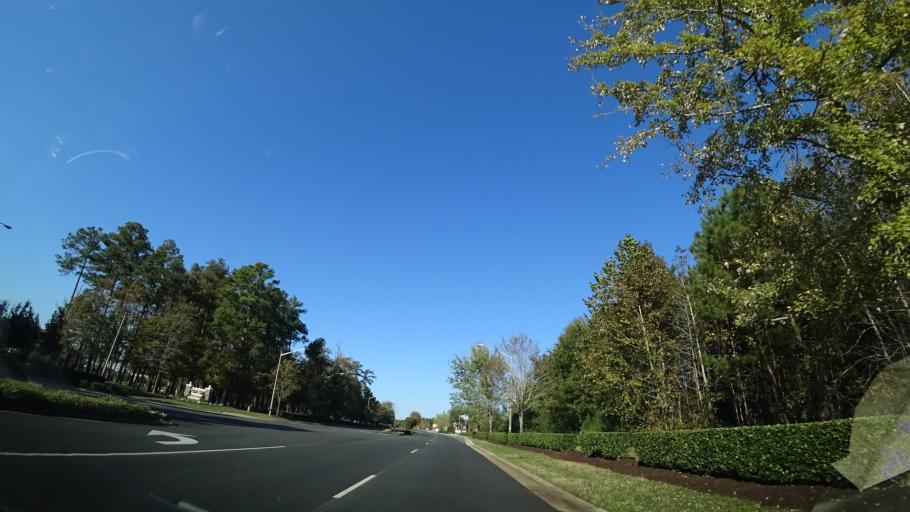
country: US
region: Virginia
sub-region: City of Portsmouth
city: Portsmouth Heights
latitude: 36.8821
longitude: -76.4369
